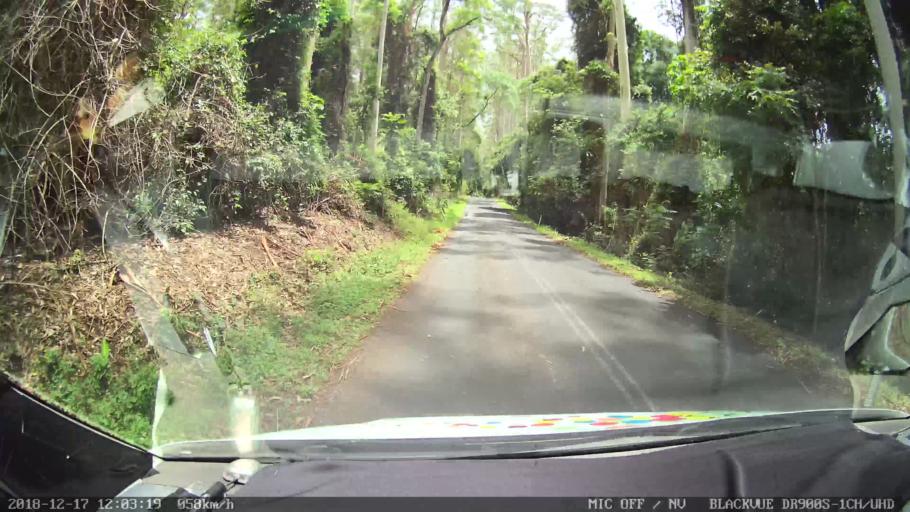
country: AU
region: New South Wales
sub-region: Kyogle
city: Kyogle
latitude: -28.5092
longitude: 152.5683
